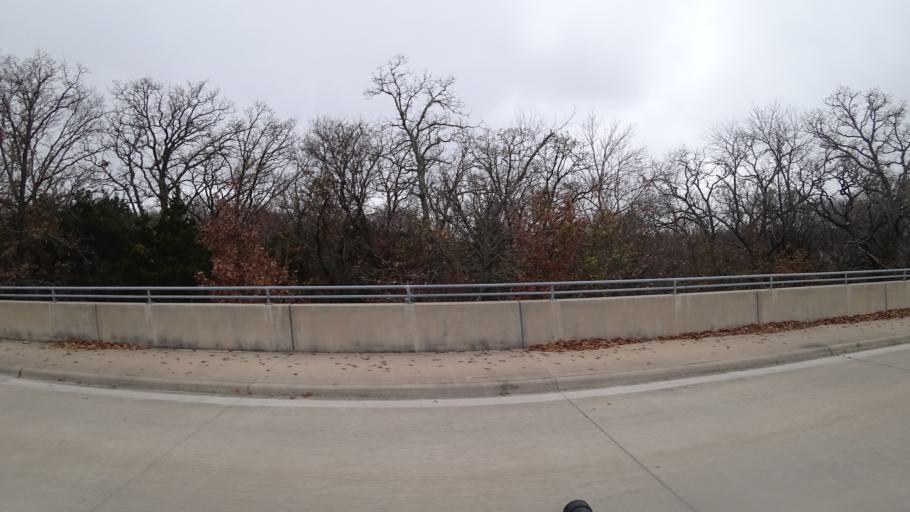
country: US
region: Texas
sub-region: Denton County
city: Lewisville
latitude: 33.0253
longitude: -97.0365
